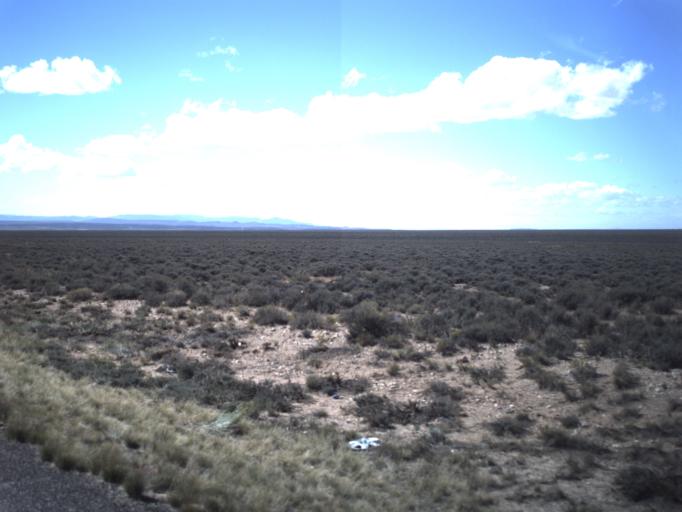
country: US
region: Utah
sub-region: Iron County
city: Enoch
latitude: 37.9453
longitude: -113.0189
